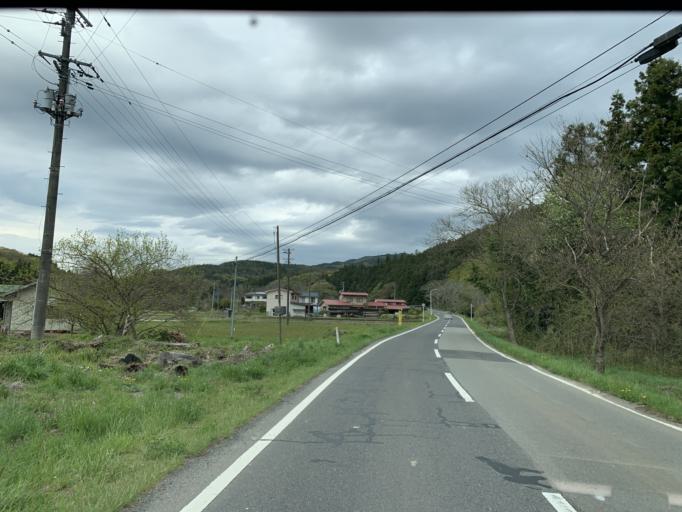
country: JP
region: Iwate
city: Ichinoseki
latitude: 38.7768
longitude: 141.3293
